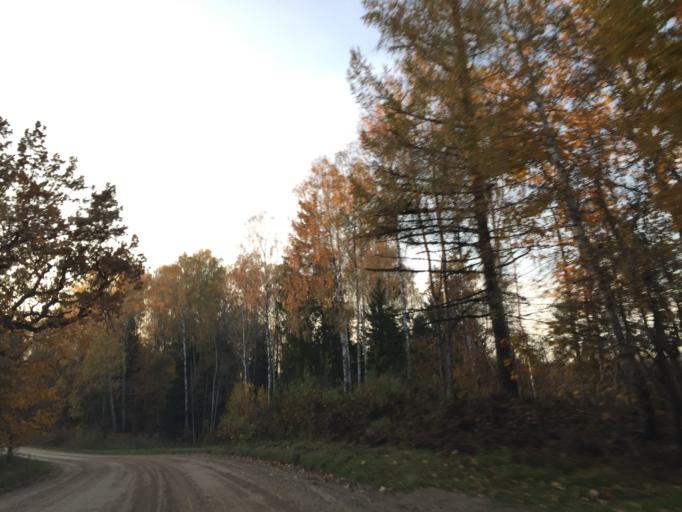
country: LV
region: Priekule
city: Priekule
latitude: 56.4802
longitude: 21.7182
